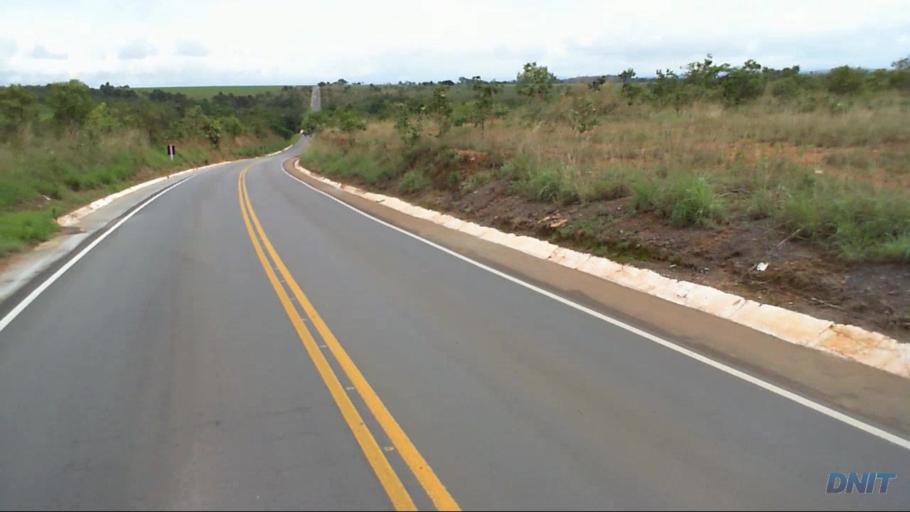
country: BR
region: Goias
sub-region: Padre Bernardo
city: Padre Bernardo
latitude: -15.3556
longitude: -48.2297
